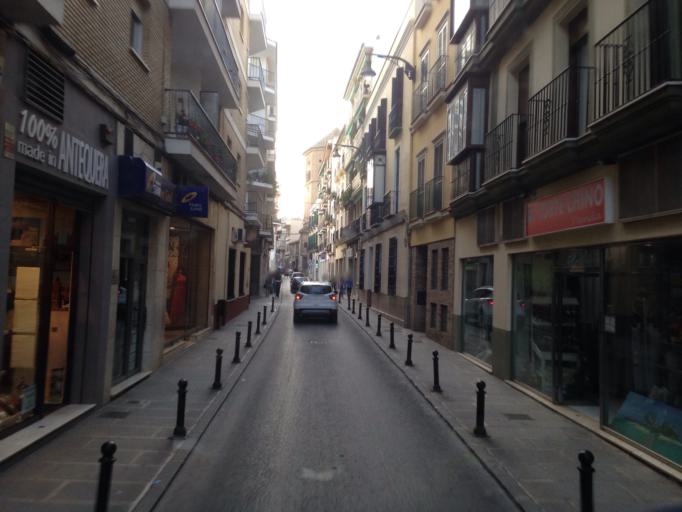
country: ES
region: Andalusia
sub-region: Provincia de Malaga
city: Antequera
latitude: 37.0189
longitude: -4.5588
